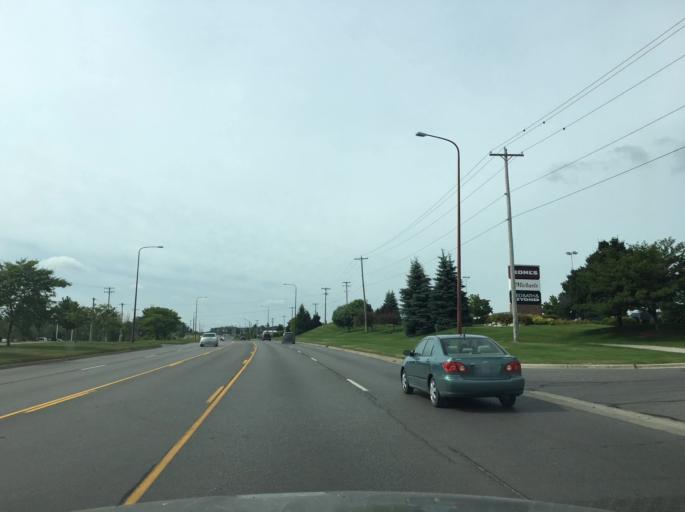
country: US
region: Michigan
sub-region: Grand Traverse County
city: Traverse City
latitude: 44.7352
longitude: -85.6461
